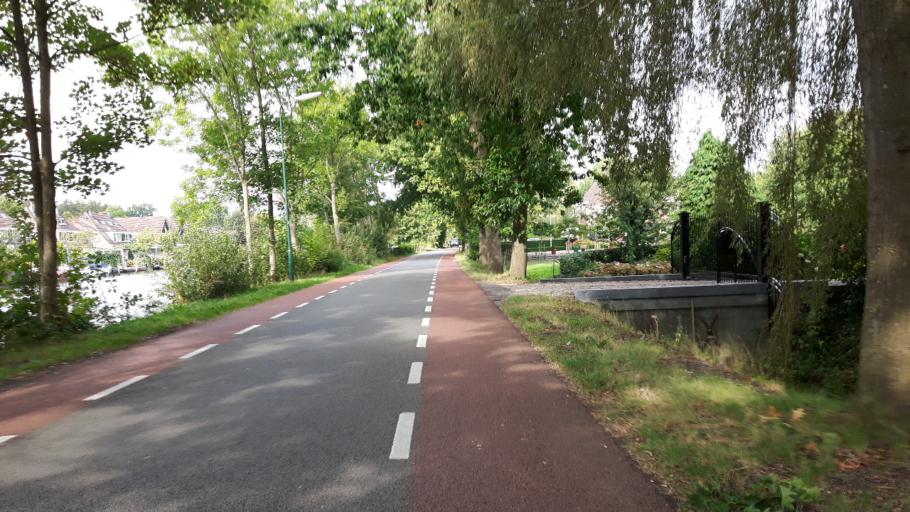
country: NL
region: Utrecht
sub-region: Stichtse Vecht
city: Breukelen
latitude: 52.1659
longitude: 5.0103
